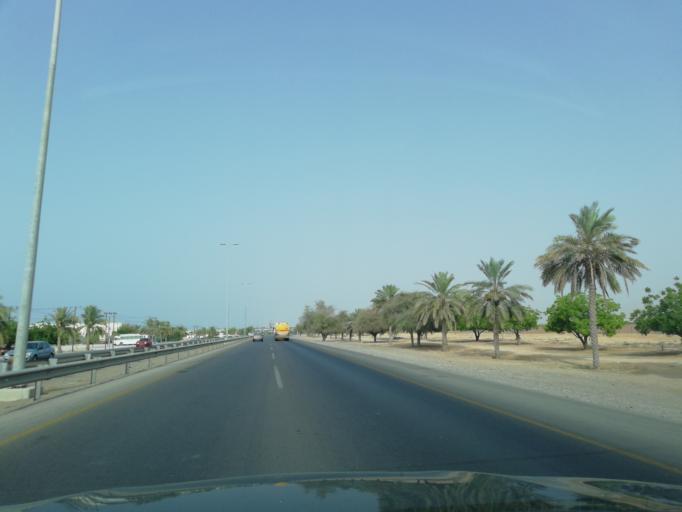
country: OM
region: Muhafazat Masqat
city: As Sib al Jadidah
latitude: 23.5898
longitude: 58.2349
